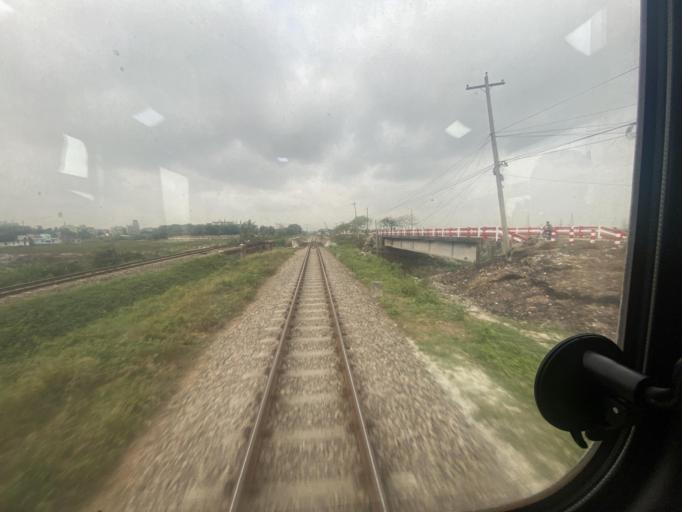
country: BD
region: Dhaka
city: Tungi
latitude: 23.9151
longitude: 90.4254
